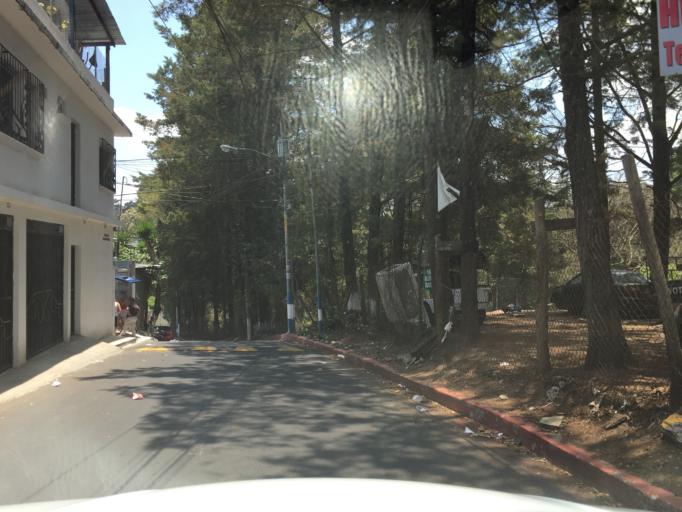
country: GT
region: Guatemala
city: Guatemala City
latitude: 14.6115
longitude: -90.5027
